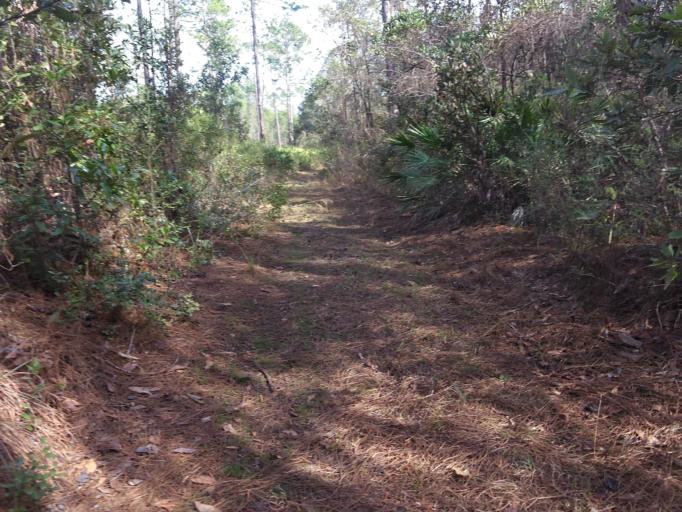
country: US
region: Florida
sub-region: Clay County
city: Middleburg
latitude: 30.1169
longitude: -81.9052
